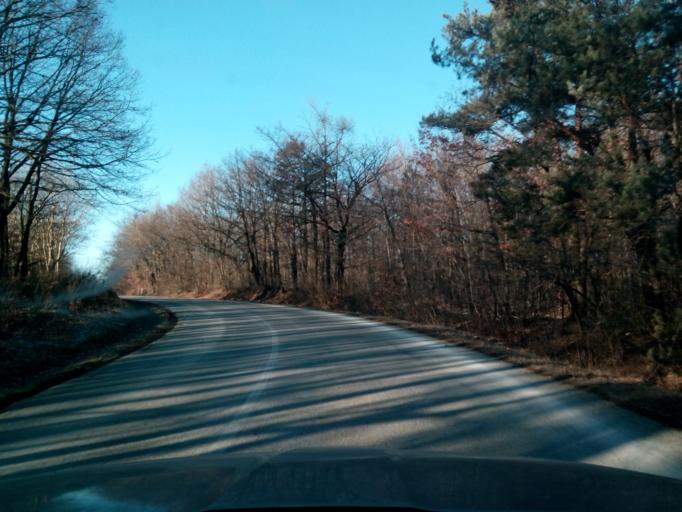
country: SK
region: Kosicky
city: Kosice
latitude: 48.6750
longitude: 21.1547
